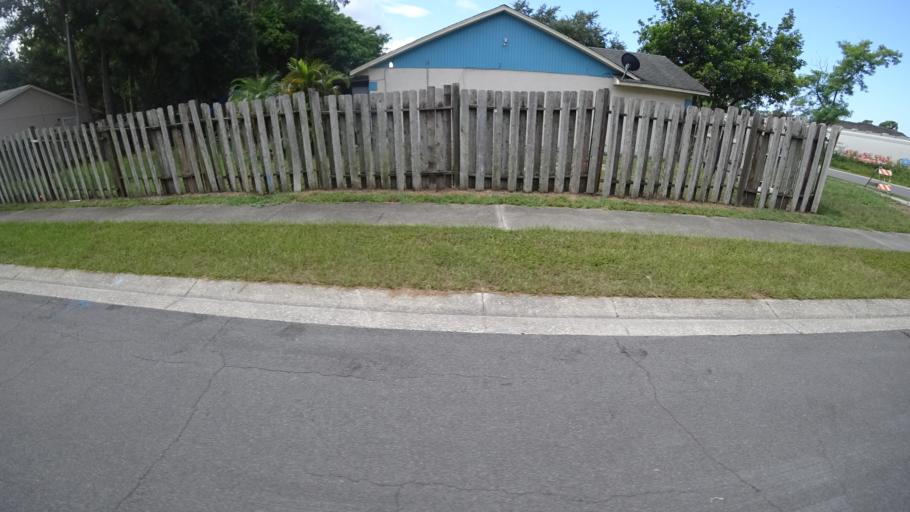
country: US
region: Florida
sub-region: Manatee County
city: Samoset
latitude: 27.4548
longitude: -82.5430
